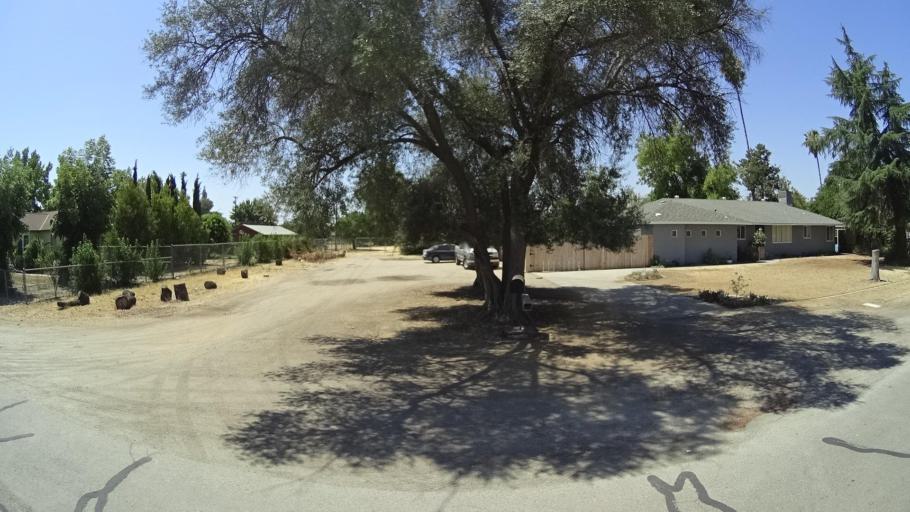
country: US
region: California
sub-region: Fresno County
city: Sunnyside
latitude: 36.7559
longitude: -119.7306
